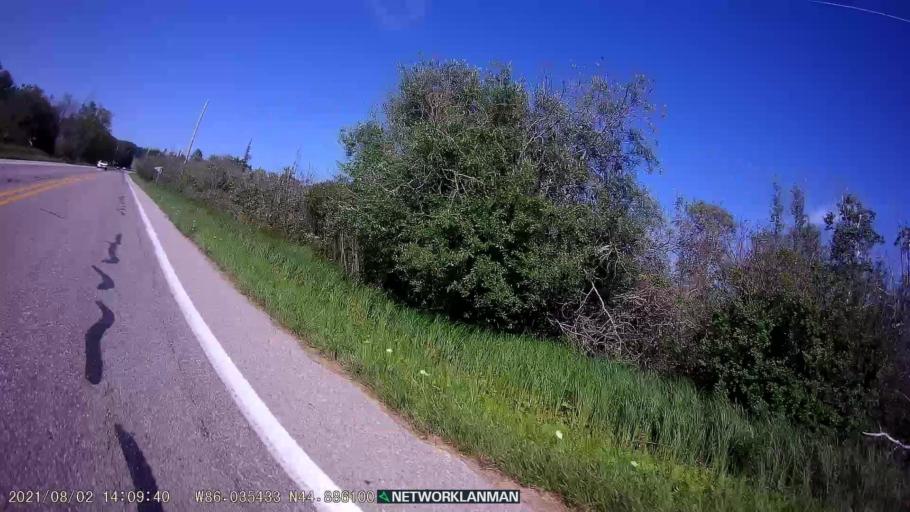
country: US
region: Michigan
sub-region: Benzie County
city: Beulah
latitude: 44.8864
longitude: -86.0353
